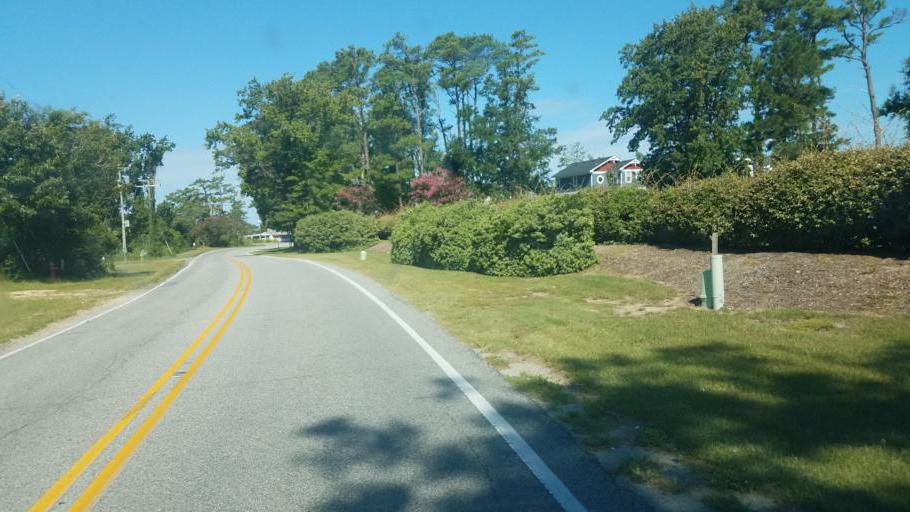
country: US
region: North Carolina
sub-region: Dare County
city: Kill Devil Hills
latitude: 36.0123
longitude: -75.6951
